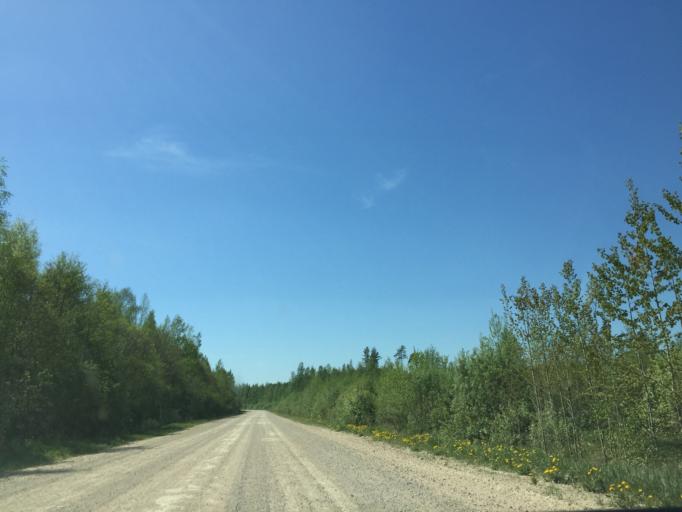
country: LV
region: Kegums
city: Kegums
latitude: 56.8805
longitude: 24.7832
